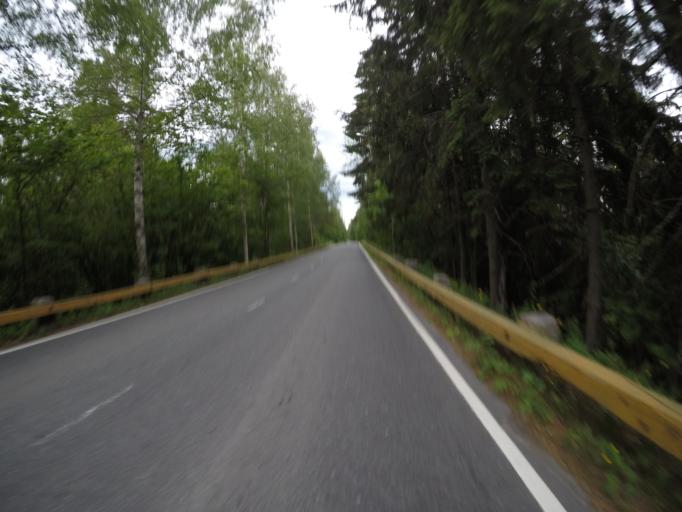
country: FI
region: Haeme
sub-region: Haemeenlinna
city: Haemeenlinna
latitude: 60.9759
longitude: 24.4606
